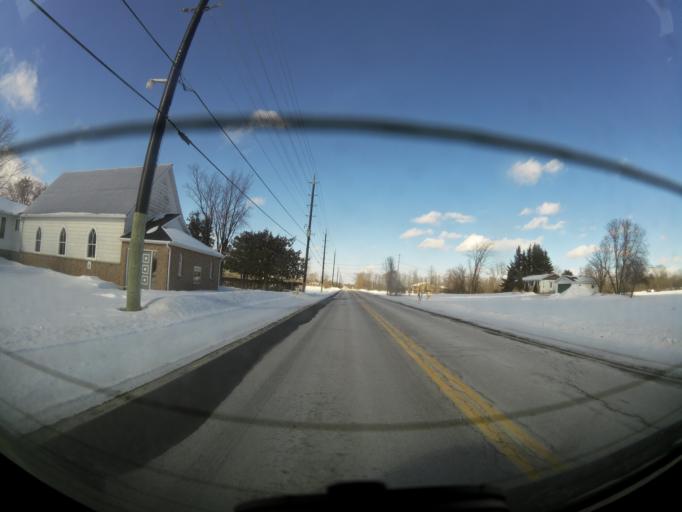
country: CA
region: Ontario
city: Ottawa
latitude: 45.2719
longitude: -75.5201
